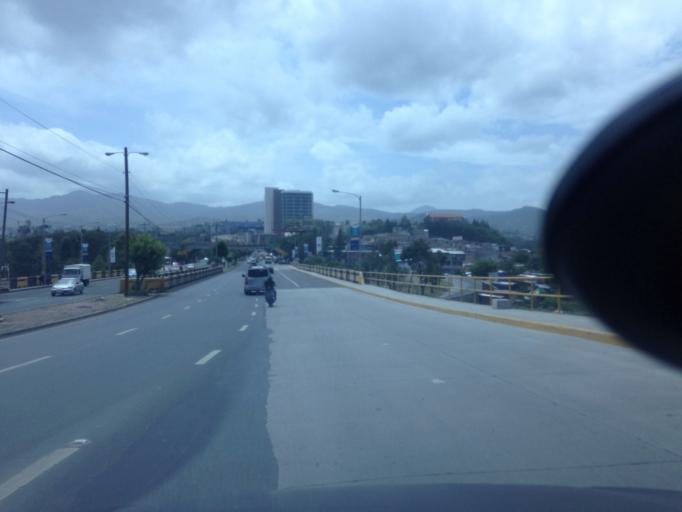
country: HN
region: Francisco Morazan
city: Tegucigalpa
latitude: 14.0721
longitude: -87.2121
